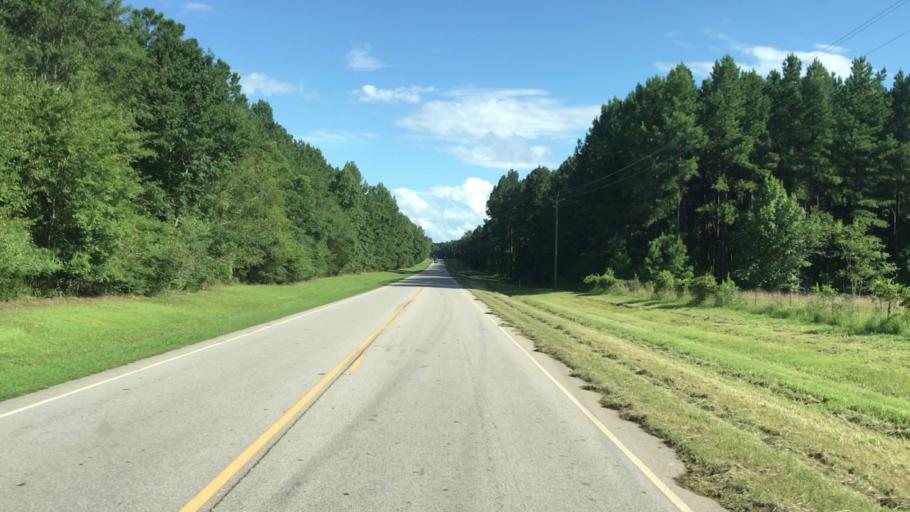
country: US
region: Georgia
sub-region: Warren County
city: Firing Range
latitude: 33.4486
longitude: -82.6952
